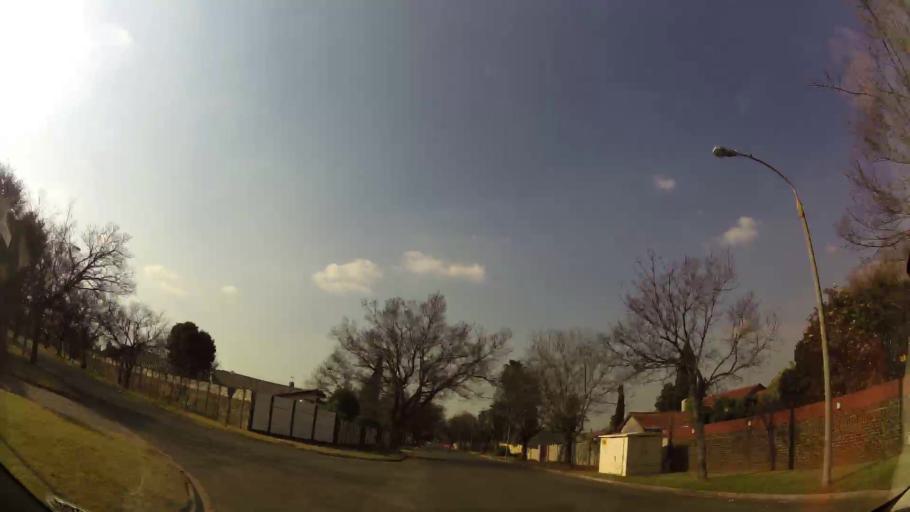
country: ZA
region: Gauteng
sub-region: Ekurhuleni Metropolitan Municipality
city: Benoni
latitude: -26.1632
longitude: 28.2815
